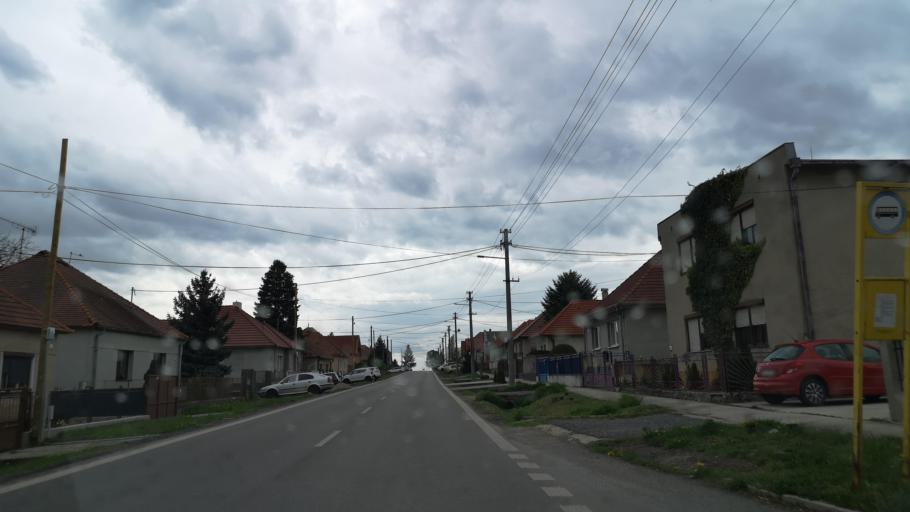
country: SK
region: Nitriansky
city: Zlate Moravce
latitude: 48.3297
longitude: 18.3511
